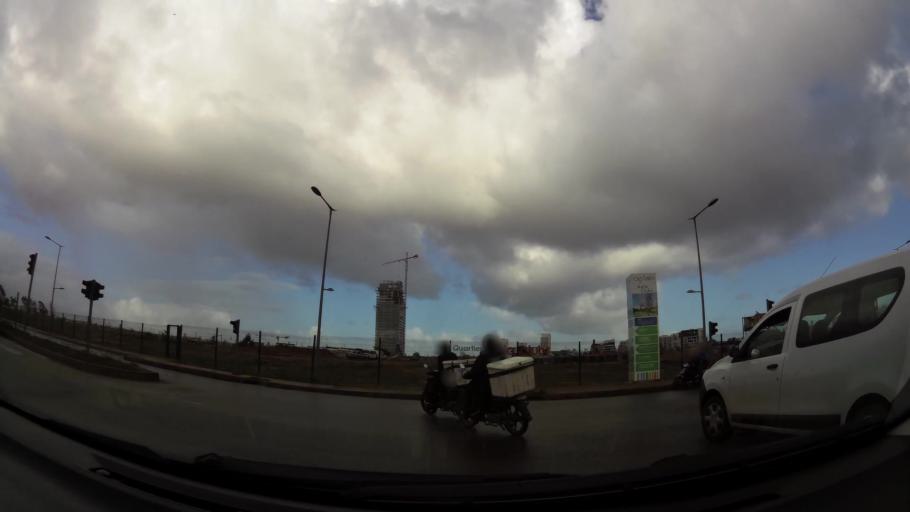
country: MA
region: Grand Casablanca
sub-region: Casablanca
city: Casablanca
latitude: 33.5629
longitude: -7.6546
